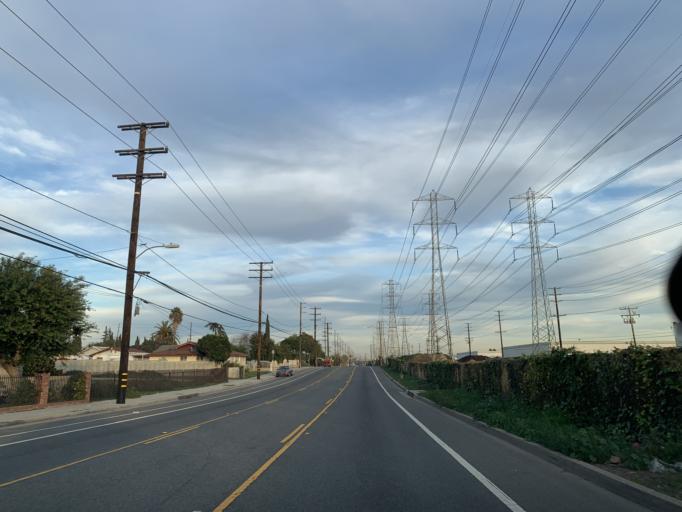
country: US
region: California
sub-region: Los Angeles County
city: Compton
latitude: 33.8809
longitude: -118.2303
